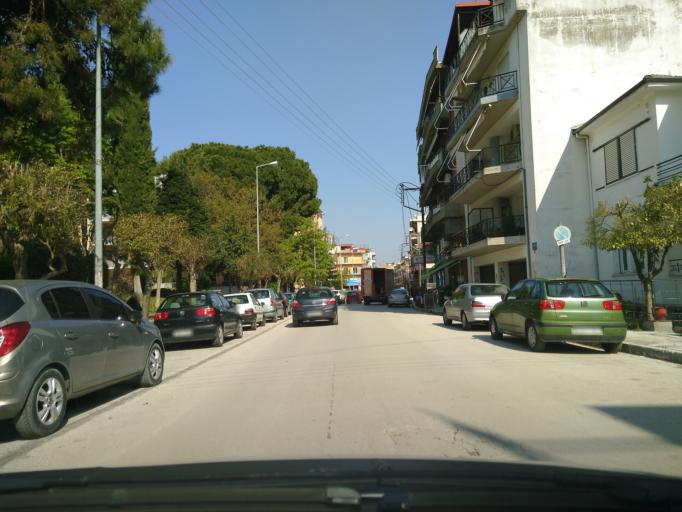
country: GR
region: Epirus
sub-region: Nomos Ioanninon
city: Ioannina
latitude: 39.6737
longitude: 20.8449
